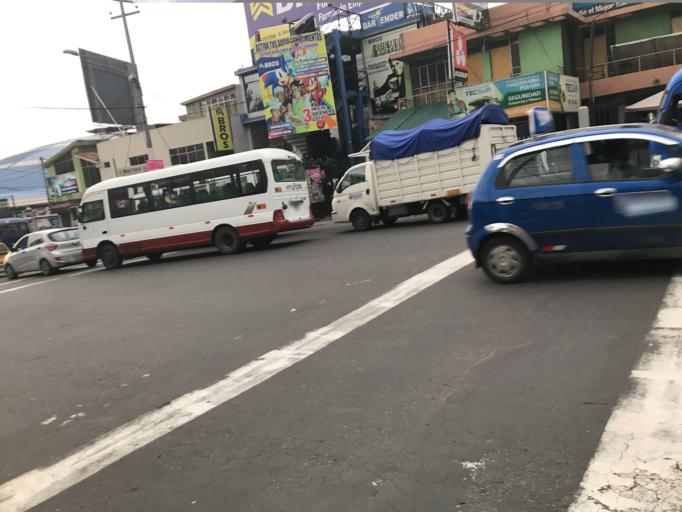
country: PE
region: Arequipa
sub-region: Provincia de Arequipa
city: Arequipa
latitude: -16.4053
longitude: -71.5286
